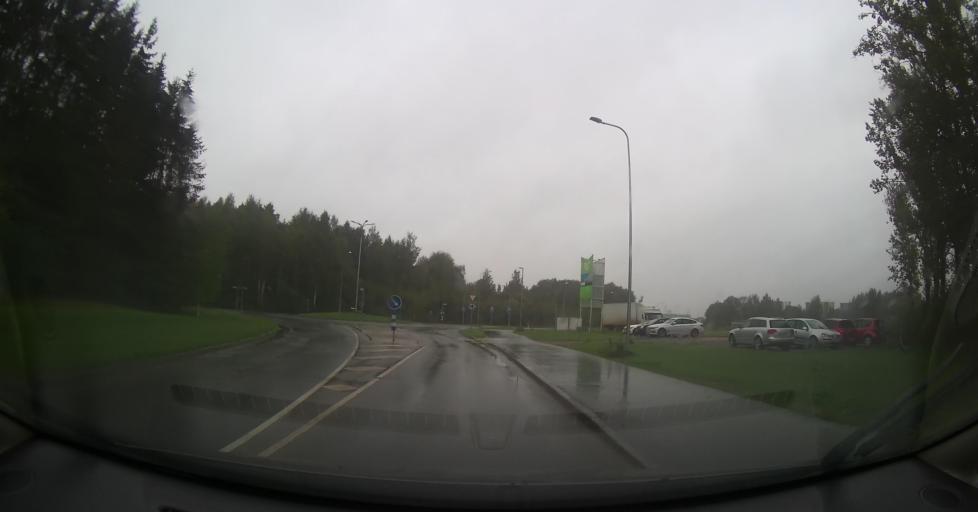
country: EE
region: Tartu
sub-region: Tartu linn
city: Tartu
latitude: 58.3669
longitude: 26.7605
